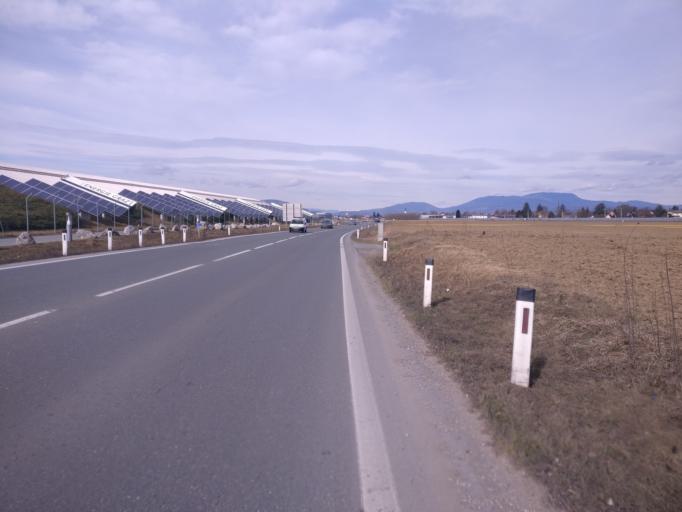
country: AT
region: Styria
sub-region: Politischer Bezirk Graz-Umgebung
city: Feldkirchen bei Graz
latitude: 46.9976
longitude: 15.4466
